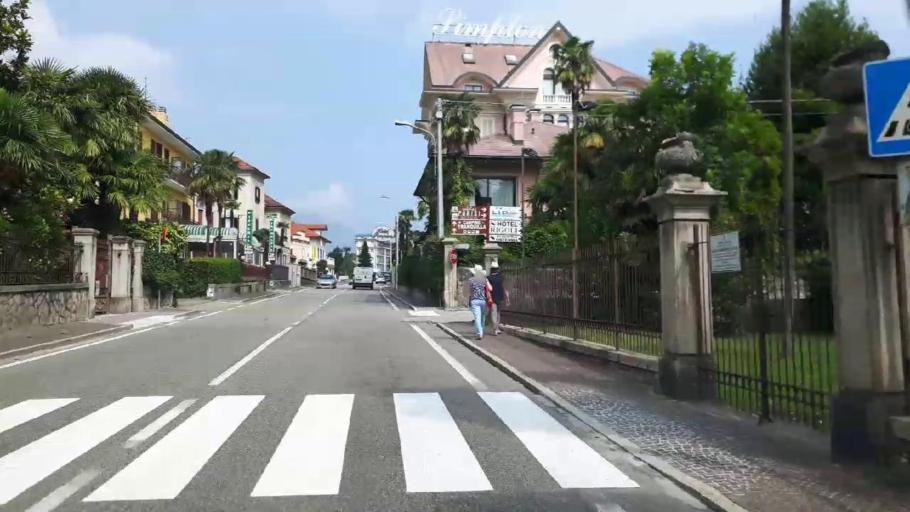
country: IT
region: Piedmont
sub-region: Provincia Verbano-Cusio-Ossola
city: Baveno
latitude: 45.9111
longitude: 8.5040
